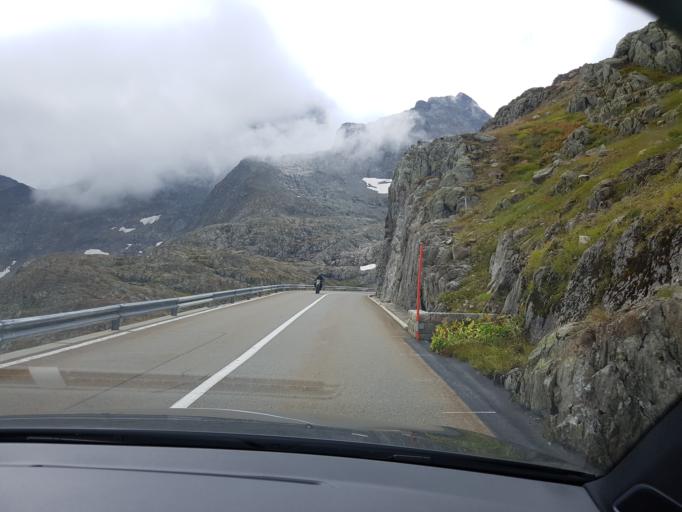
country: CH
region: Obwalden
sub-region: Obwalden
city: Engelberg
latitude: 46.7325
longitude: 8.4514
